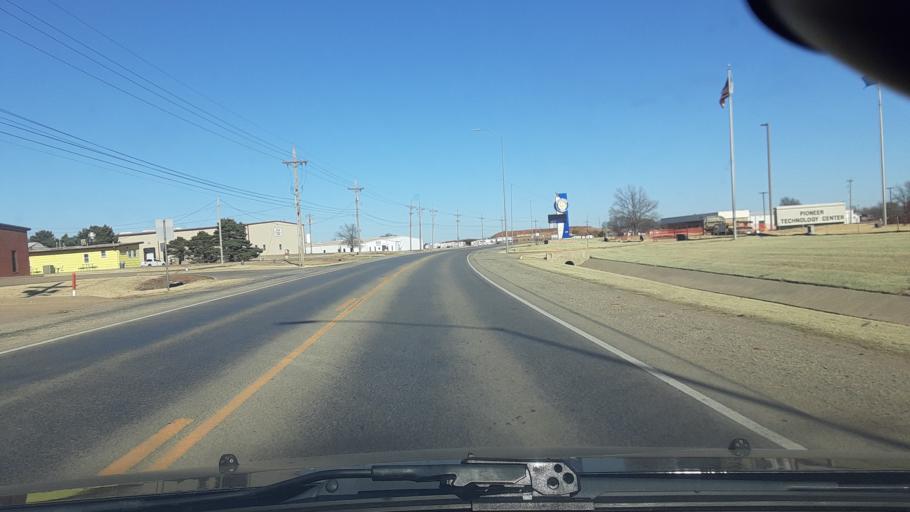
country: US
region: Oklahoma
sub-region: Kay County
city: Ponca City
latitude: 36.7277
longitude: -97.0949
